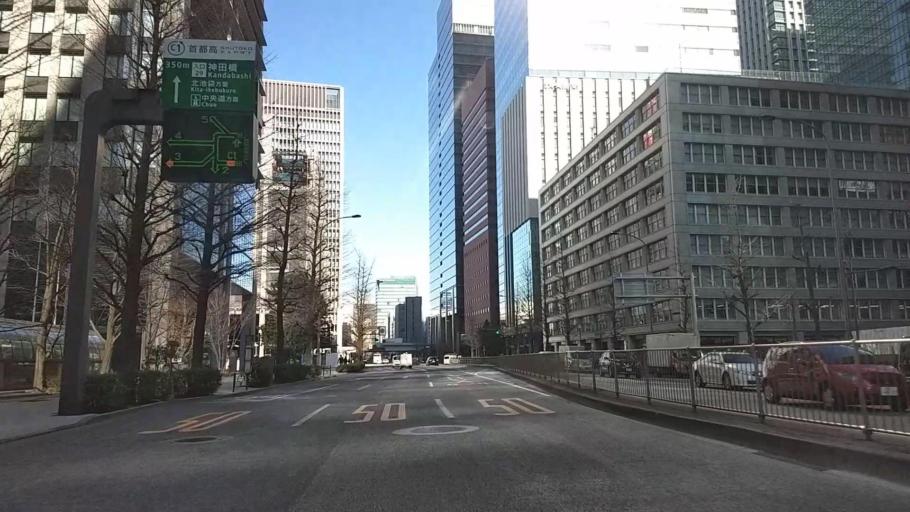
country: JP
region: Tokyo
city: Tokyo
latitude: 35.6859
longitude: 139.7633
